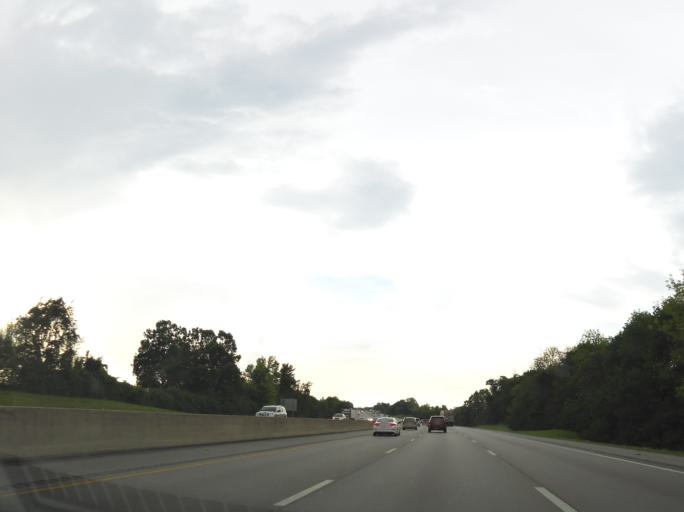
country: US
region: Kentucky
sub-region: Fayette County
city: Lexington
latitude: 37.9817
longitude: -84.3890
